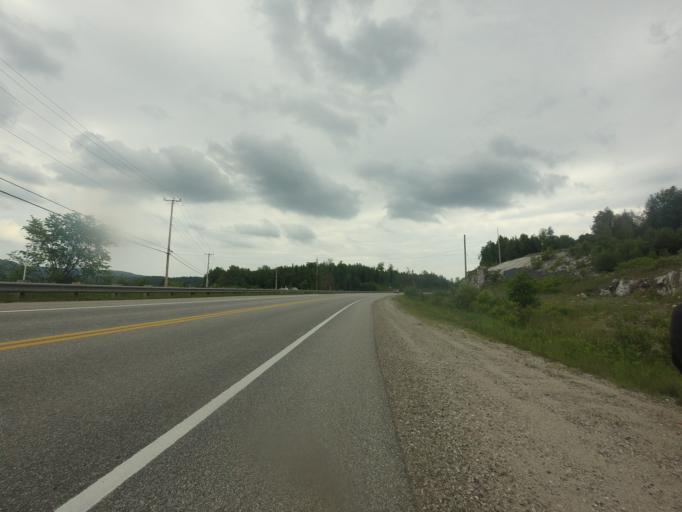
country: CA
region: Quebec
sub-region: Outaouais
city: Wakefield
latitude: 45.7317
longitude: -75.9074
